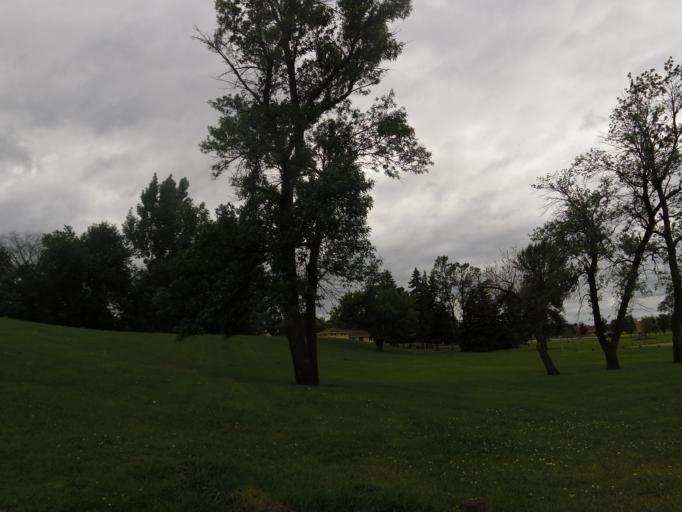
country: US
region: North Dakota
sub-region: Walsh County
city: Grafton
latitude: 48.4206
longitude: -97.4168
